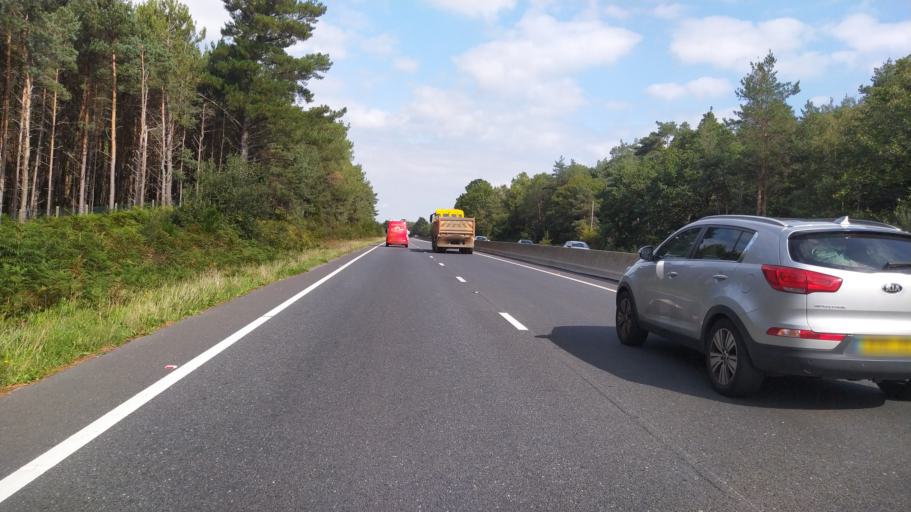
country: GB
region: England
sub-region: Hampshire
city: Ringwood
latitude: 50.8283
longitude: -1.8108
